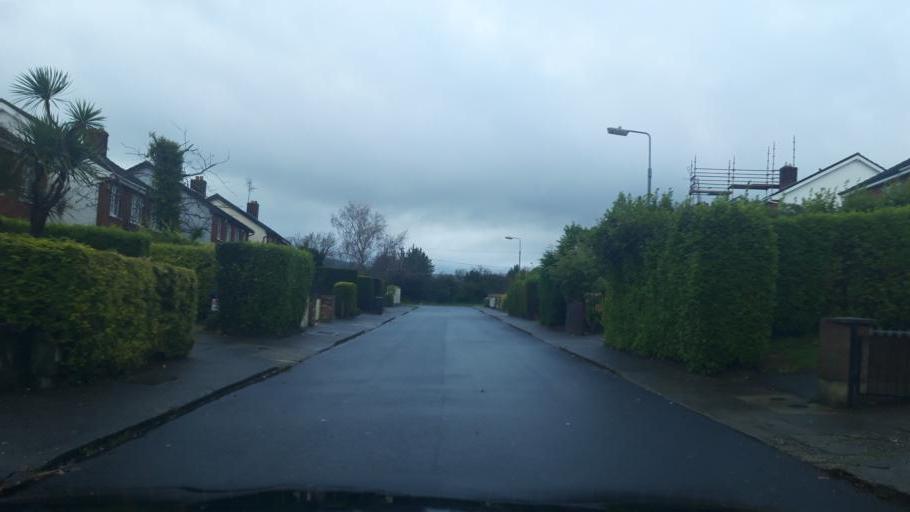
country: IE
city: Newtownmountkennedy
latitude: 53.0931
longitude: -6.1156
